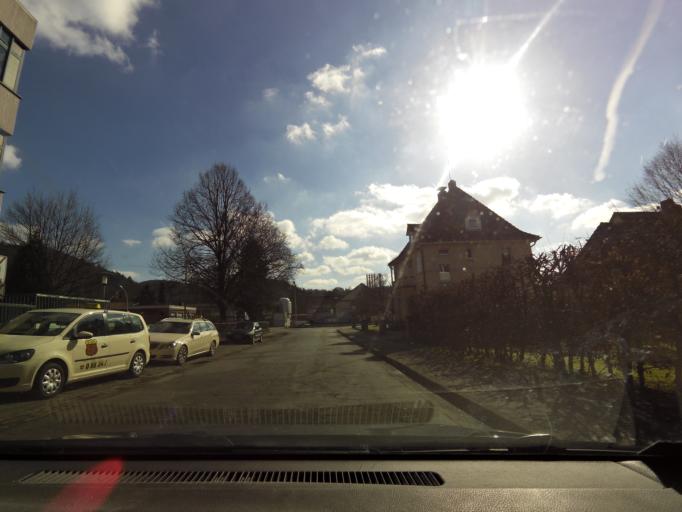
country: DE
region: Lower Saxony
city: Bad Lauterberg im Harz
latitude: 51.6263
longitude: 10.4625
